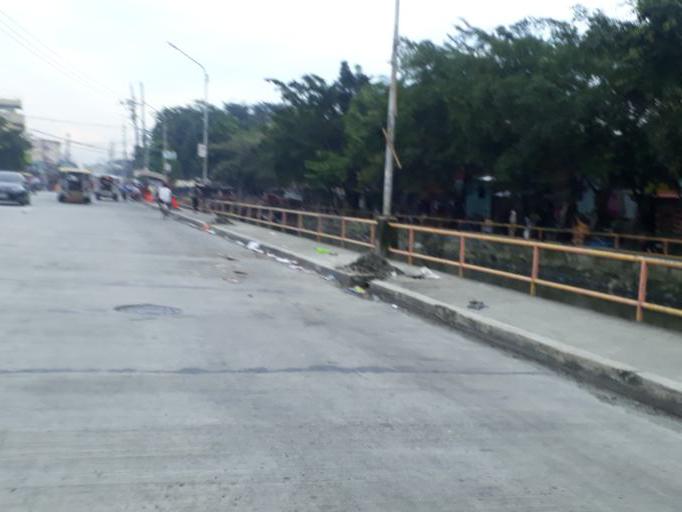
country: PH
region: Metro Manila
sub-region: Caloocan City
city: Niugan
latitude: 14.6596
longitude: 120.9608
